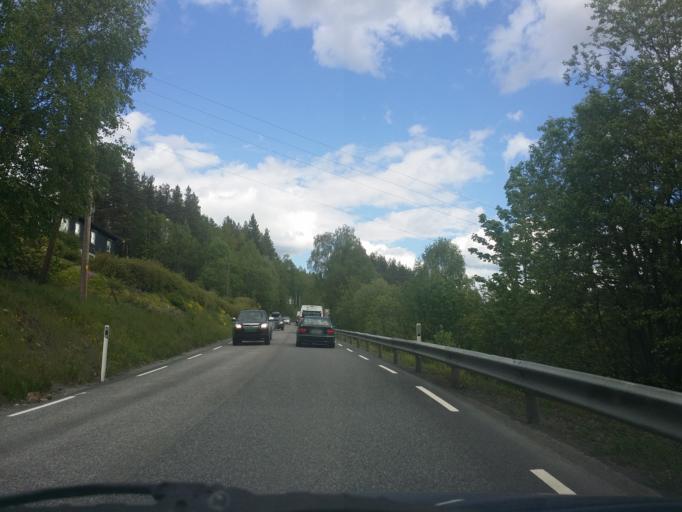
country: NO
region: Oppland
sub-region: Jevnaker
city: Jevnaker
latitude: 60.2671
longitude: 10.4675
